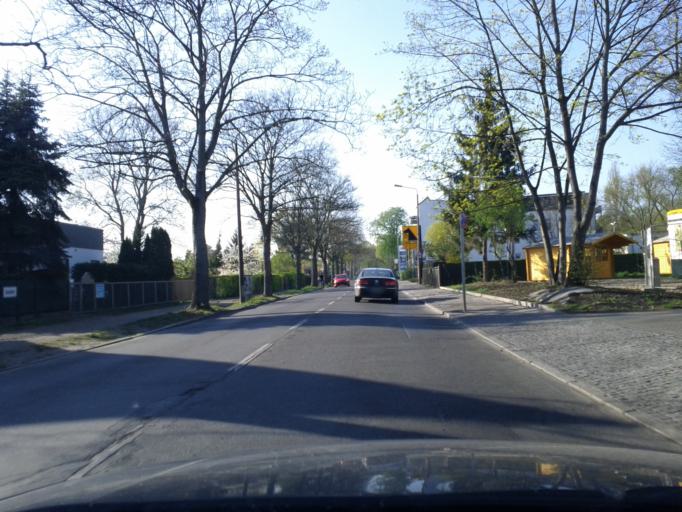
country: DE
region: Berlin
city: Wilhelmsruh
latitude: 52.5754
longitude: 13.3797
